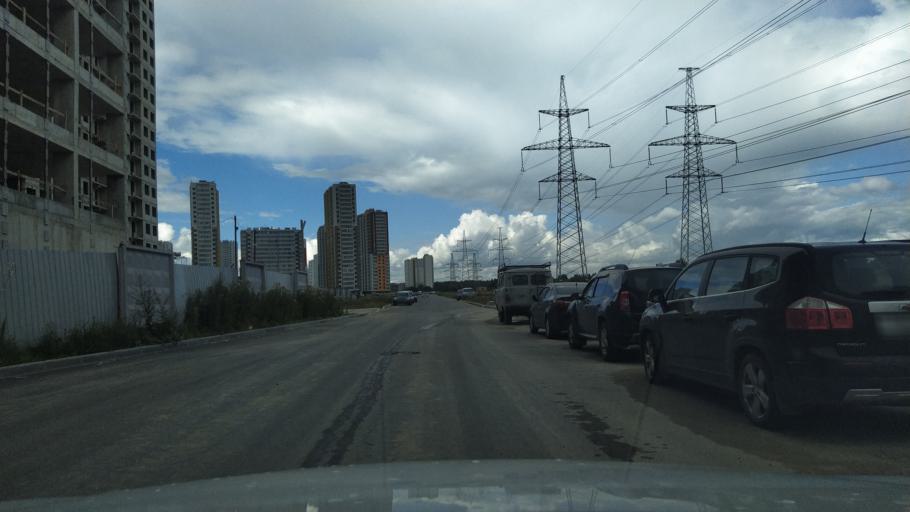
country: RU
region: St.-Petersburg
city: Krasnogvargeisky
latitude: 60.0032
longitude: 30.4831
